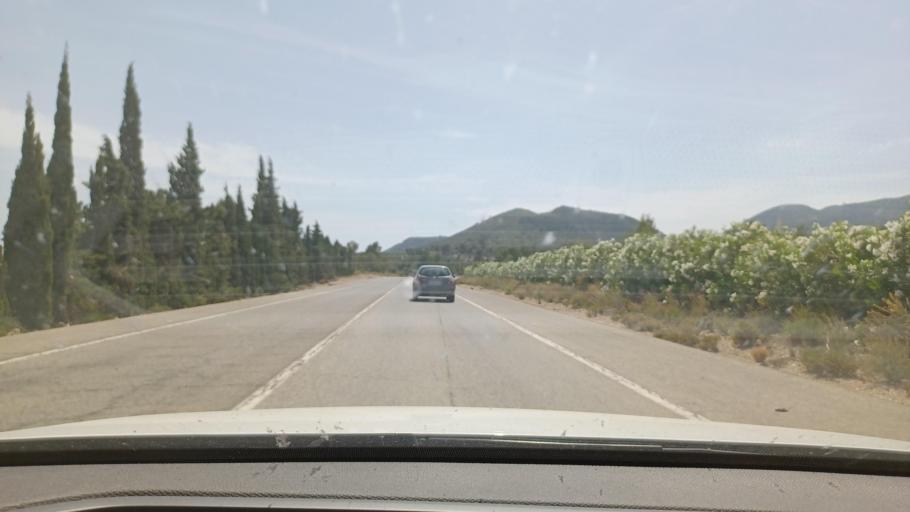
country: ES
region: Catalonia
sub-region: Provincia de Tarragona
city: Colldejou
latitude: 40.9822
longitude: 0.9017
